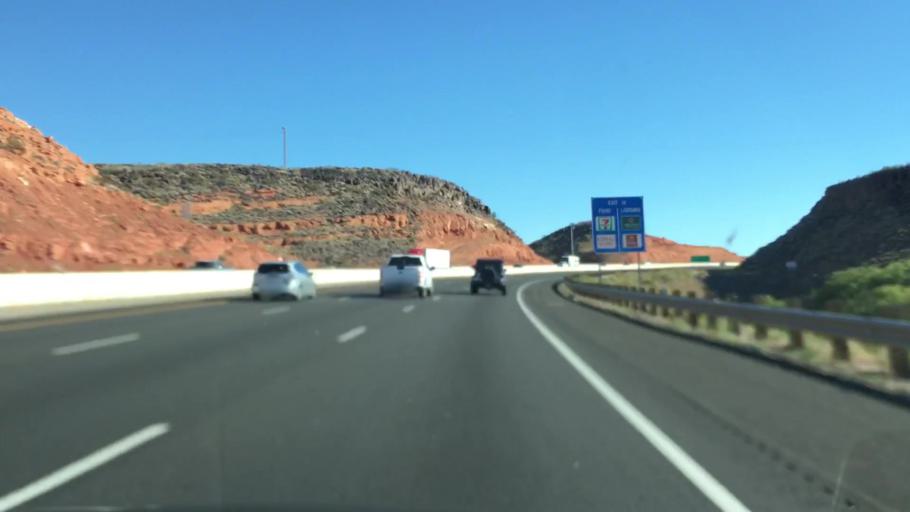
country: US
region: Utah
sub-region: Washington County
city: Washington
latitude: 37.1571
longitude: -113.4763
